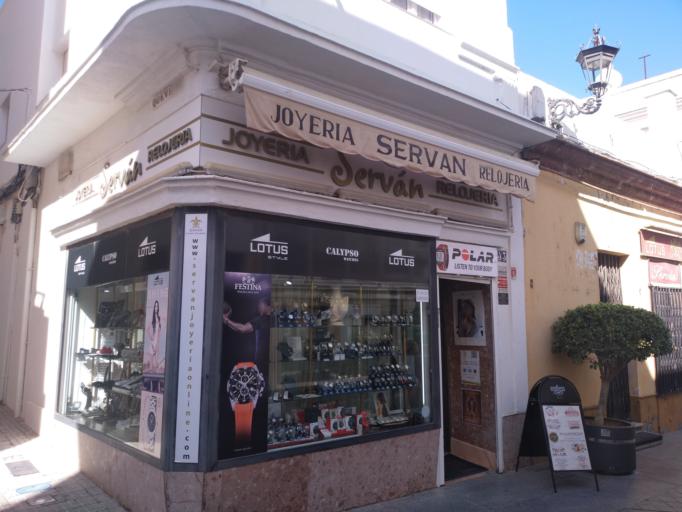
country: ES
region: Andalusia
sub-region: Provincia de Cadiz
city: San Fernando
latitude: 36.4670
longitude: -6.1965
